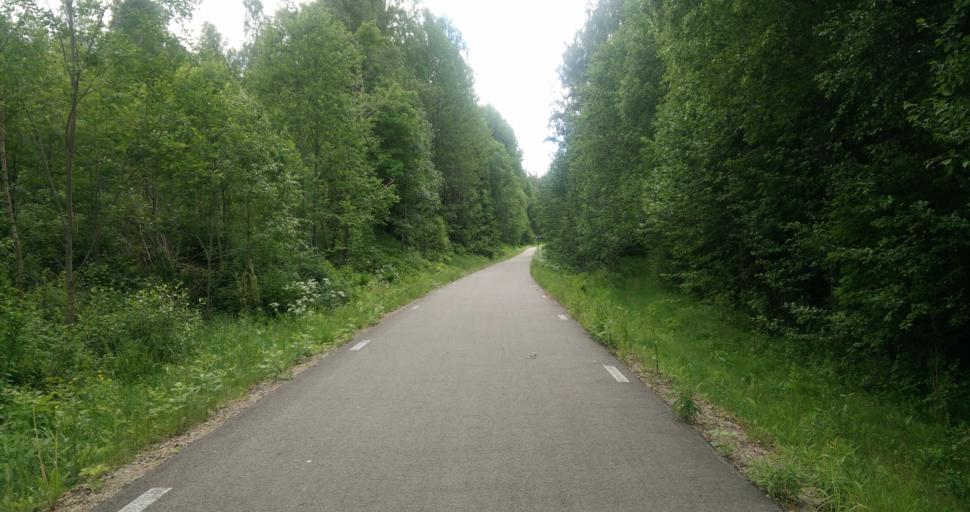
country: SE
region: Vaermland
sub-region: Hagfors Kommun
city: Hagfors
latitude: 59.9936
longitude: 13.5890
